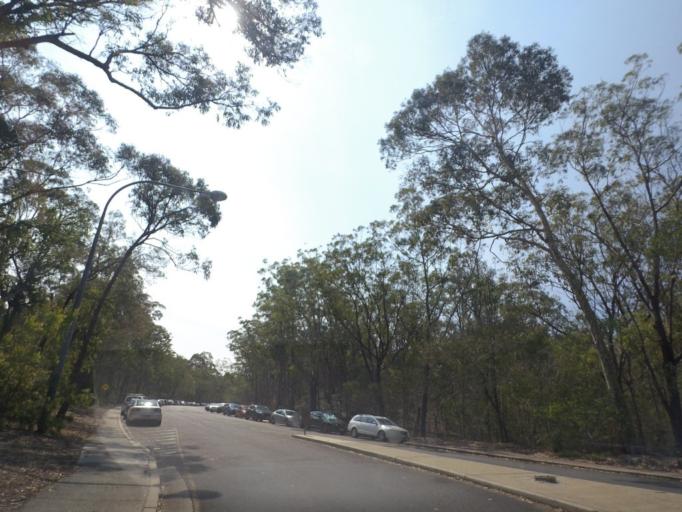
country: AU
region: Queensland
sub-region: Brisbane
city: Nathan
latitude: -27.5508
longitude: 153.0576
